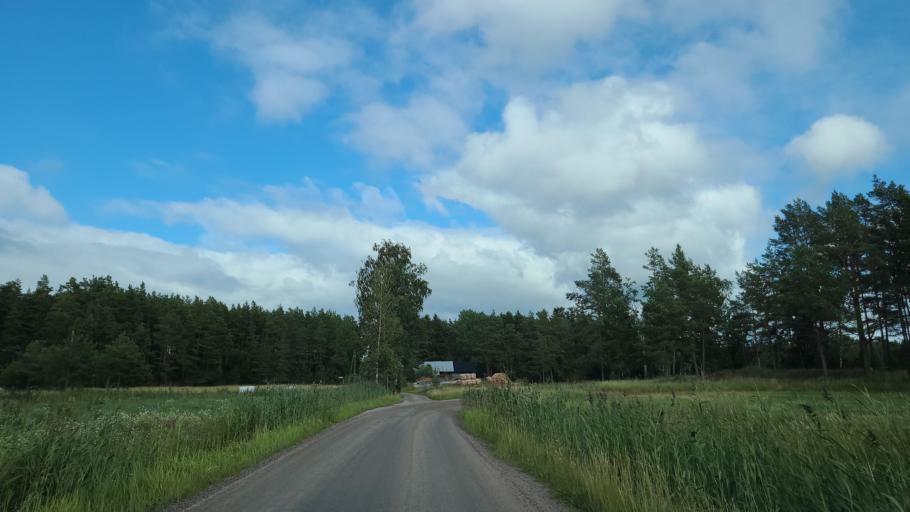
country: FI
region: Varsinais-Suomi
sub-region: Aboland-Turunmaa
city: Nagu
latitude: 60.1518
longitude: 21.7678
